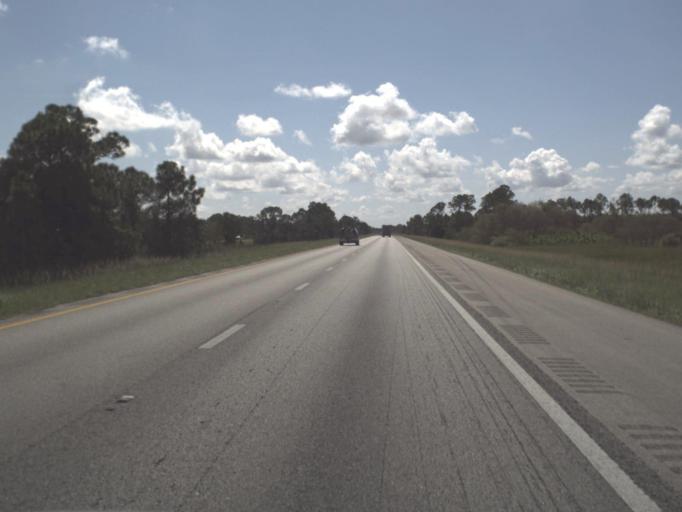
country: US
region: Florida
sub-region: Lee County
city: Burnt Store Marina
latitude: 26.8200
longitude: -81.9430
